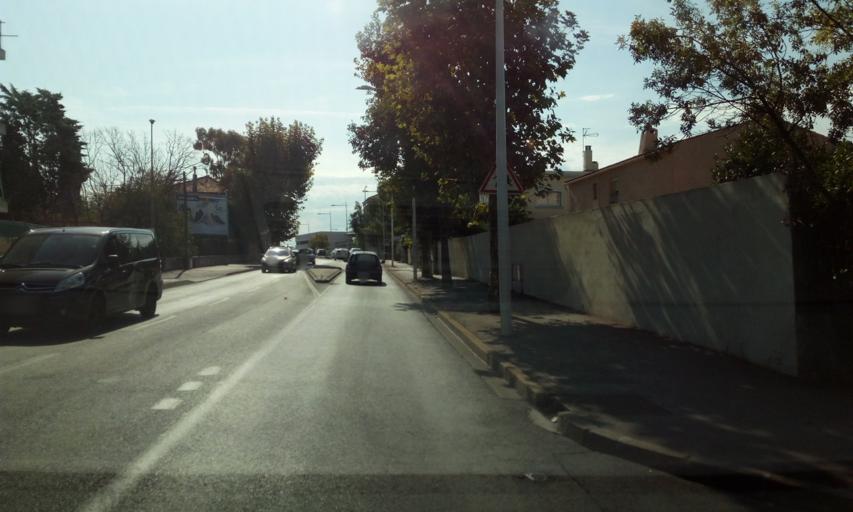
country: FR
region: Provence-Alpes-Cote d'Azur
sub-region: Departement du Var
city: La Valette-du-Var
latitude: 43.1202
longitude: 5.9766
